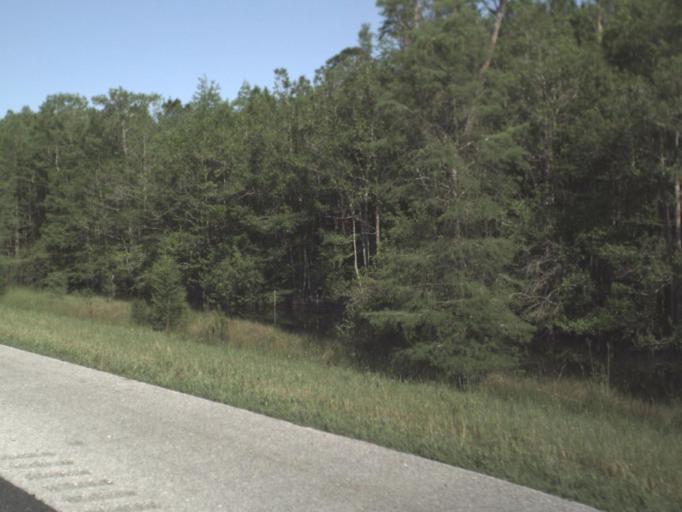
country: US
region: Florida
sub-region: Holmes County
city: Bonifay
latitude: 30.7630
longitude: -85.7157
